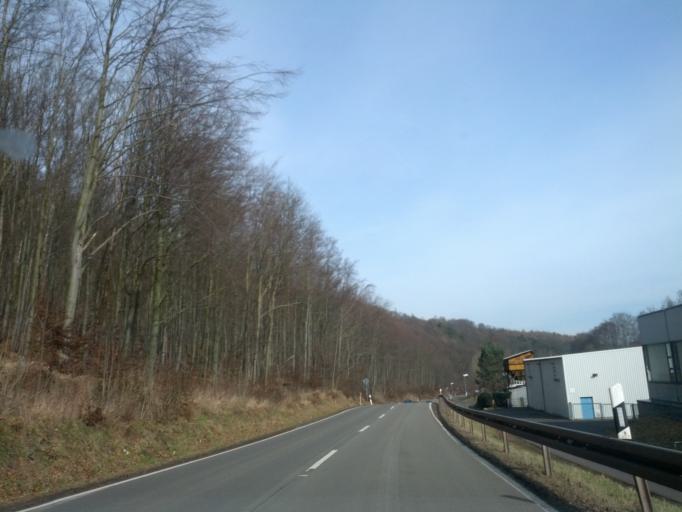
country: DE
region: Thuringia
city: Ruhla
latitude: 50.9076
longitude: 10.3755
